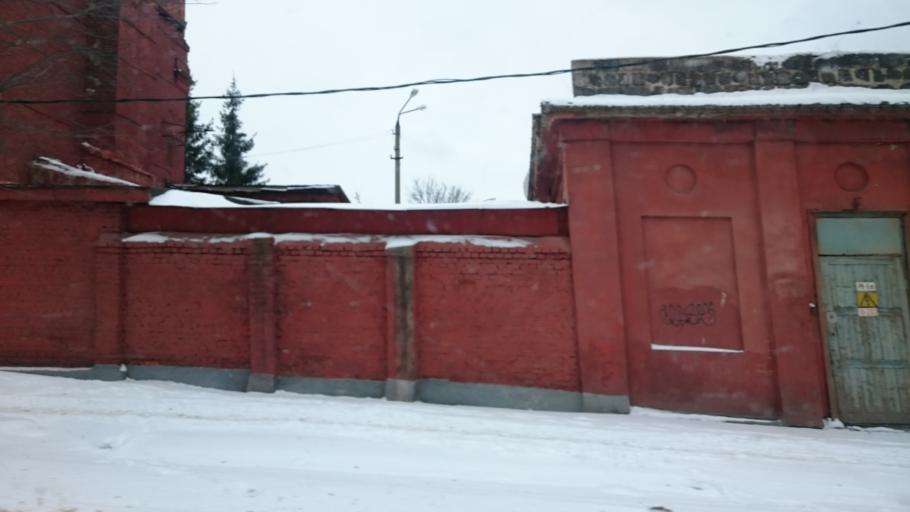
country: RU
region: Tula
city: Tula
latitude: 54.1987
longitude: 37.6313
